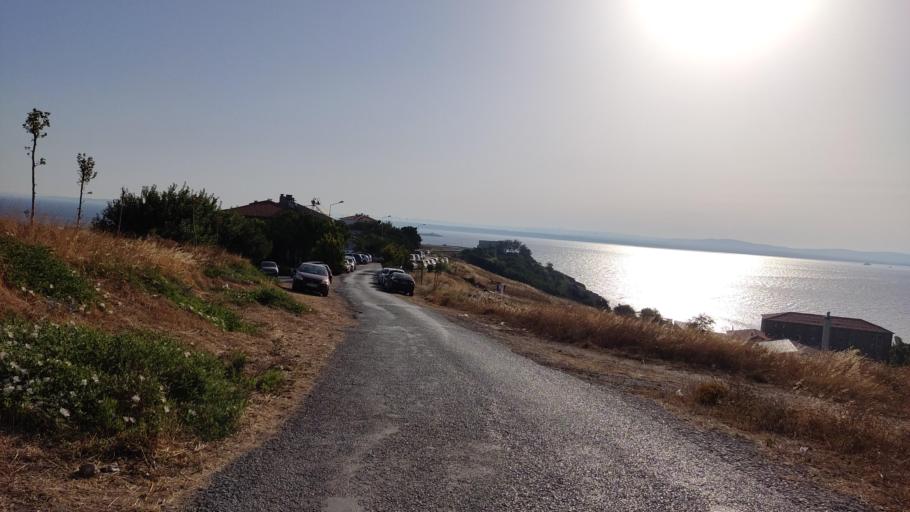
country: TR
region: Canakkale
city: Bozcaada
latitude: 39.8312
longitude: 26.0706
